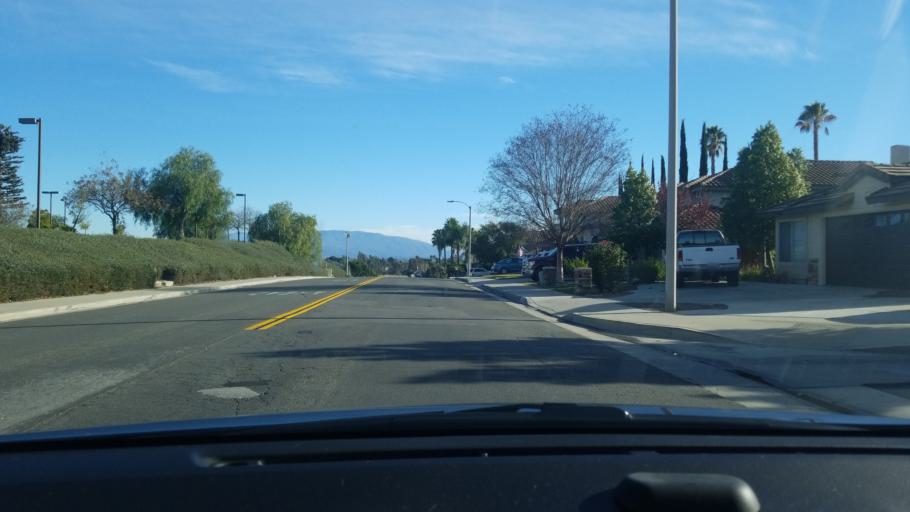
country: US
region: California
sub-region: Riverside County
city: Murrieta
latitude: 33.5691
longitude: -117.1957
